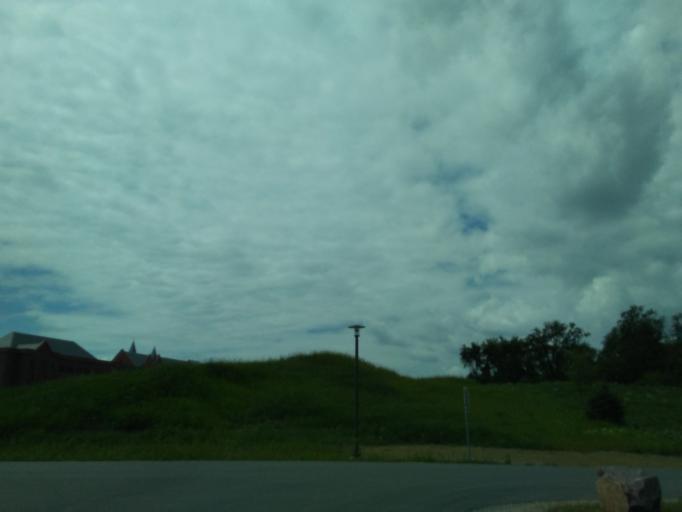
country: US
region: Wisconsin
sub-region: Dane County
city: Verona
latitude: 43.0015
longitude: -89.5626
